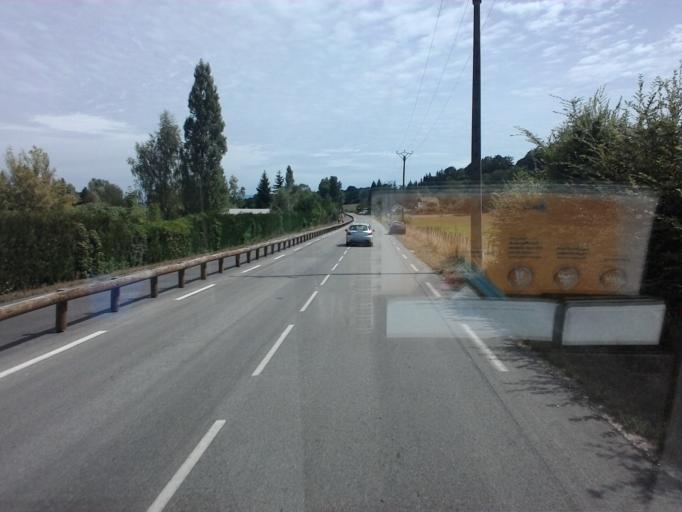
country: FR
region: Rhone-Alpes
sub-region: Departement de l'Isere
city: Bilieu
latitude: 45.4674
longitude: 5.5590
